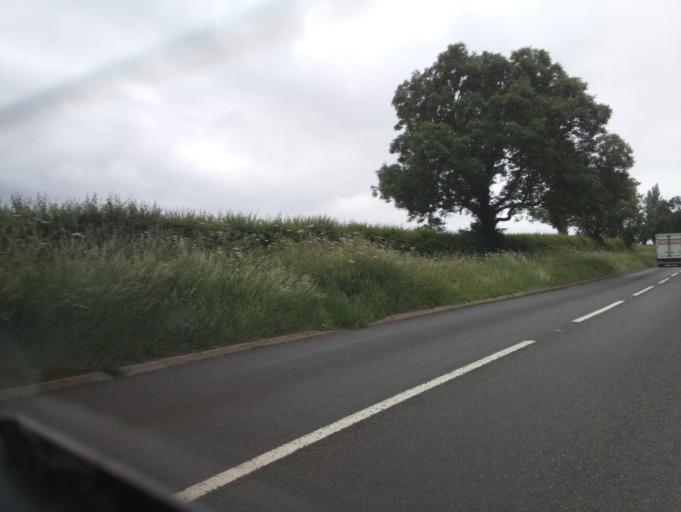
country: GB
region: England
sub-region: District of Rutland
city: Preston
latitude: 52.6033
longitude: -0.7213
